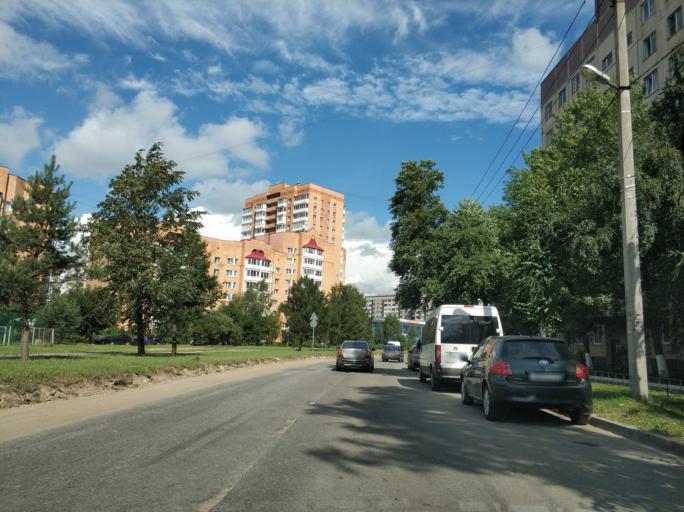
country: RU
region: Leningrad
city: Vsevolozhsk
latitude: 60.0268
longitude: 30.6264
